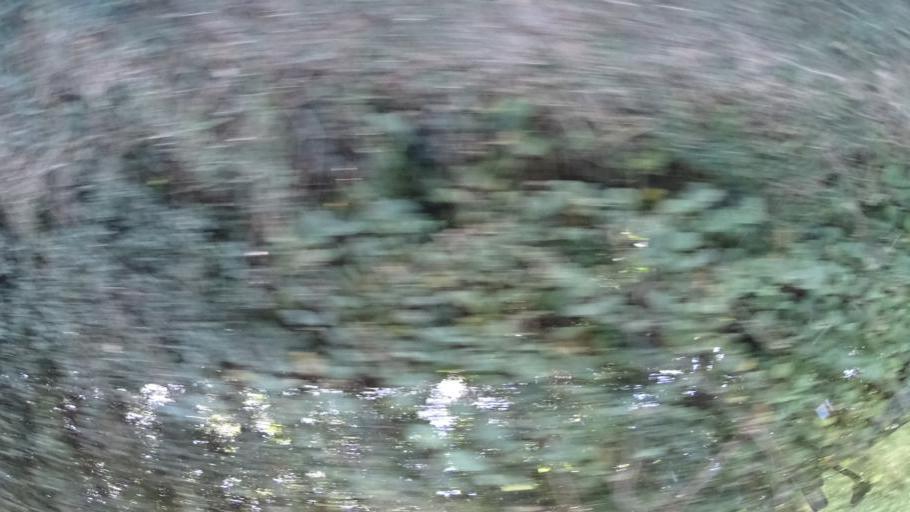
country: DE
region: Baden-Wuerttemberg
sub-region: Karlsruhe Region
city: Ubstadt-Weiher
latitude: 49.1301
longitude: 8.6511
